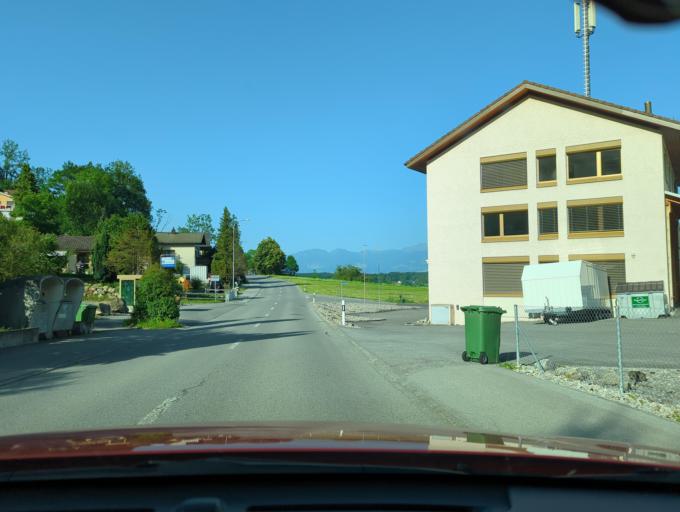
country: CH
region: Saint Gallen
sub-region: Wahlkreis Werdenberg
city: Gams
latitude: 47.2351
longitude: 9.4596
